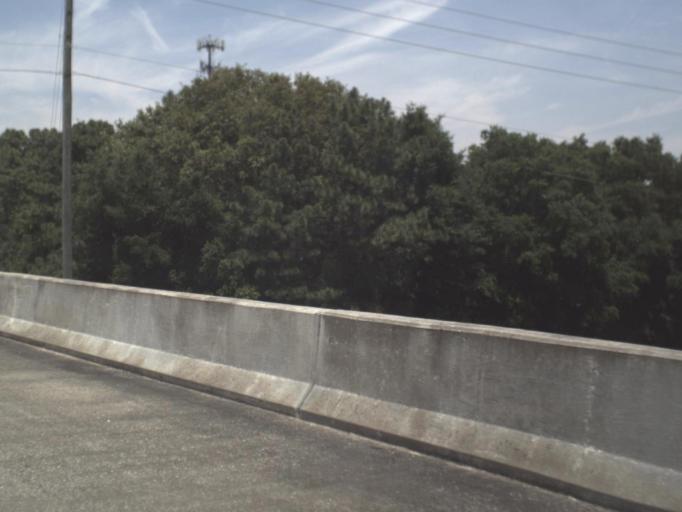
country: US
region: Florida
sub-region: Duval County
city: Jacksonville
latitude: 30.3408
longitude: -81.5415
